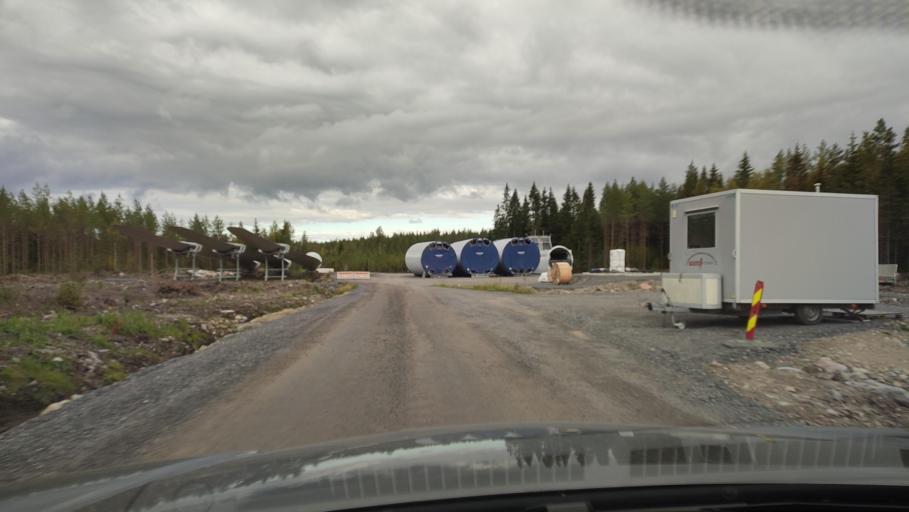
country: FI
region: Southern Ostrobothnia
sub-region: Suupohja
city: Karijoki
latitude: 62.2036
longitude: 21.5863
